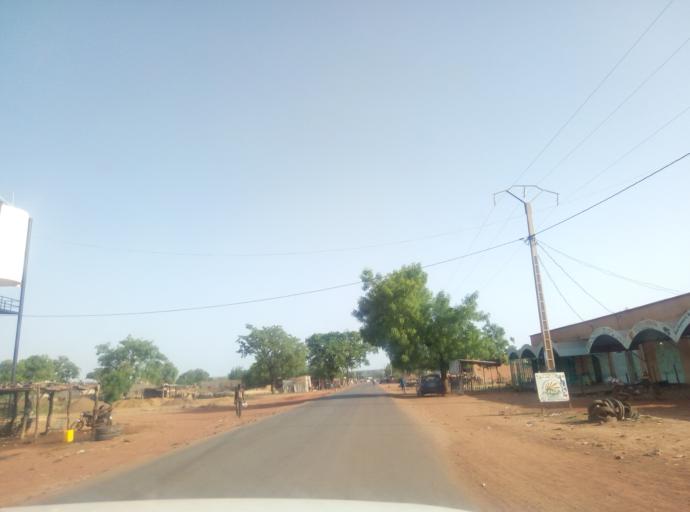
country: ML
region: Bamako
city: Bamako
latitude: 12.5934
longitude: -7.7666
